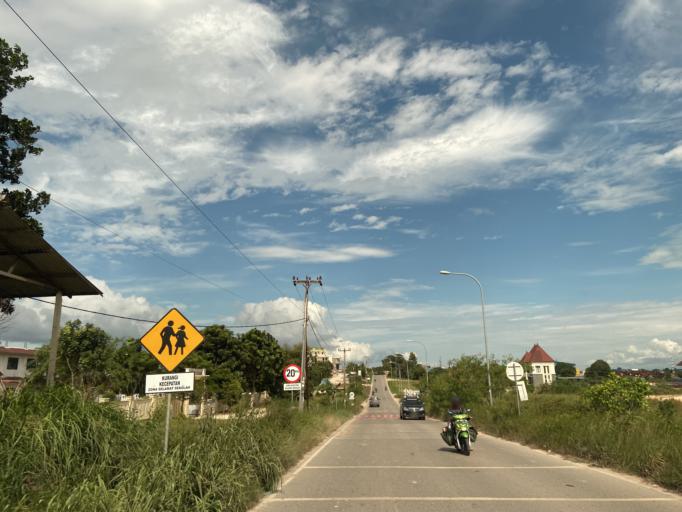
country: SG
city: Singapore
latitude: 1.0321
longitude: 103.9410
